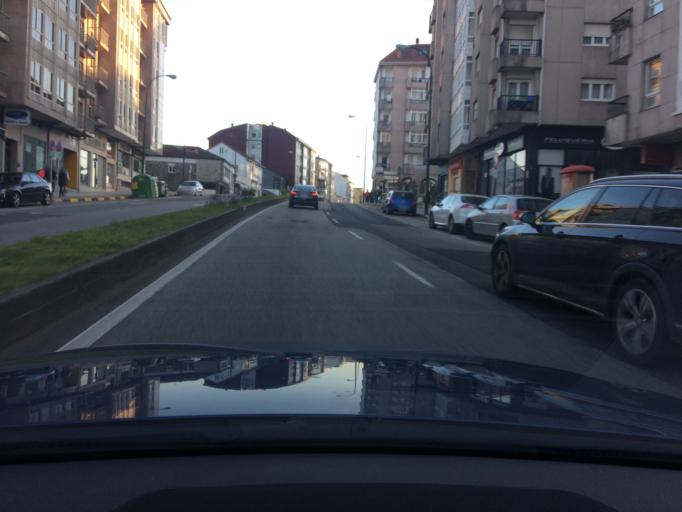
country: ES
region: Galicia
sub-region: Provincia da Coruna
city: Santiago de Compostela
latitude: 42.8435
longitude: -8.5775
